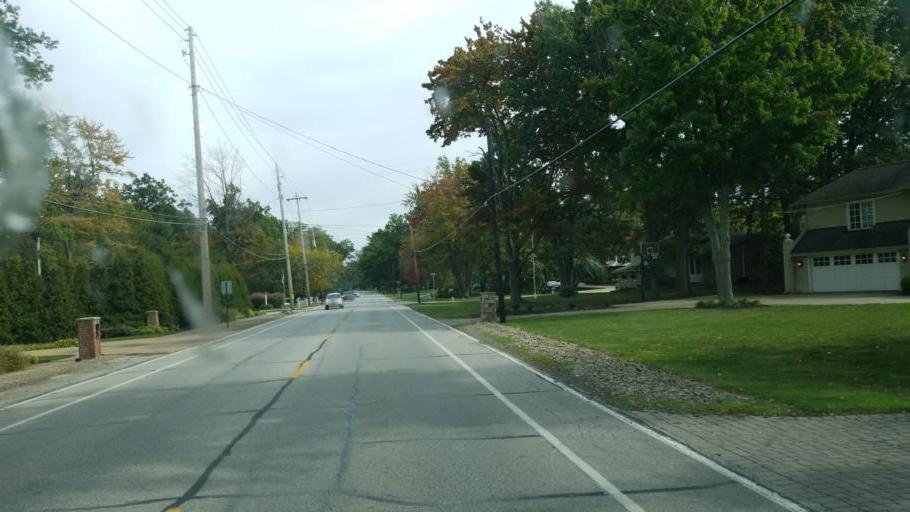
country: US
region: Ohio
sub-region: Lorain County
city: Avon Lake
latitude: 41.5071
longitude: -81.9776
